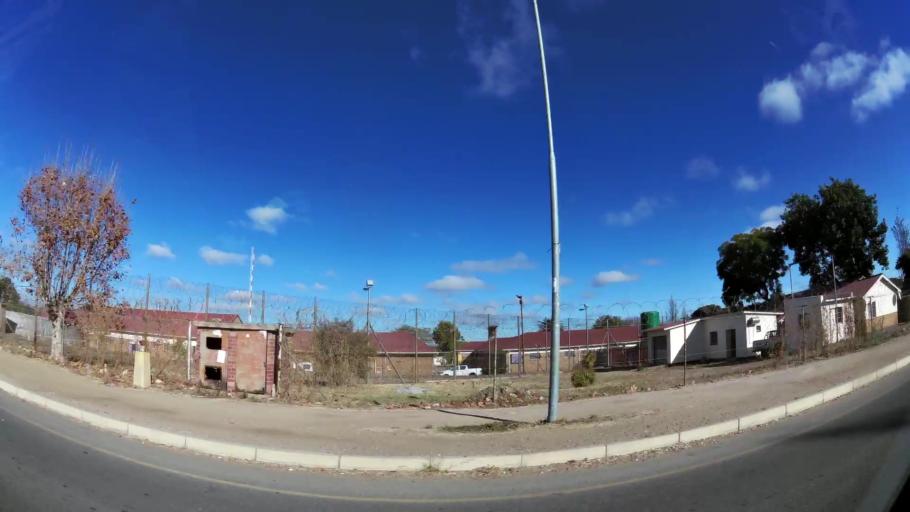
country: ZA
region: Limpopo
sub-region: Capricorn District Municipality
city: Polokwane
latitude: -23.8960
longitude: 29.4532
